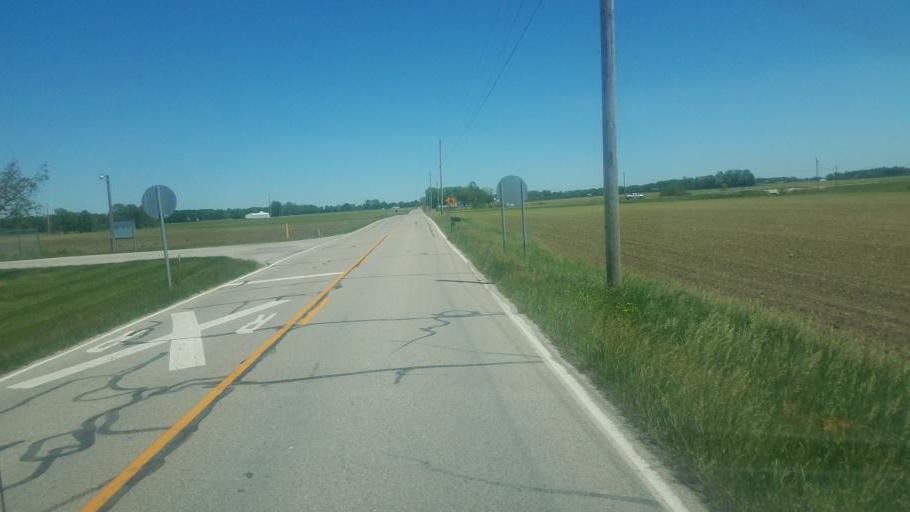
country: US
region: Ohio
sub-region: Shelby County
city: Sidney
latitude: 40.2159
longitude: -84.1940
